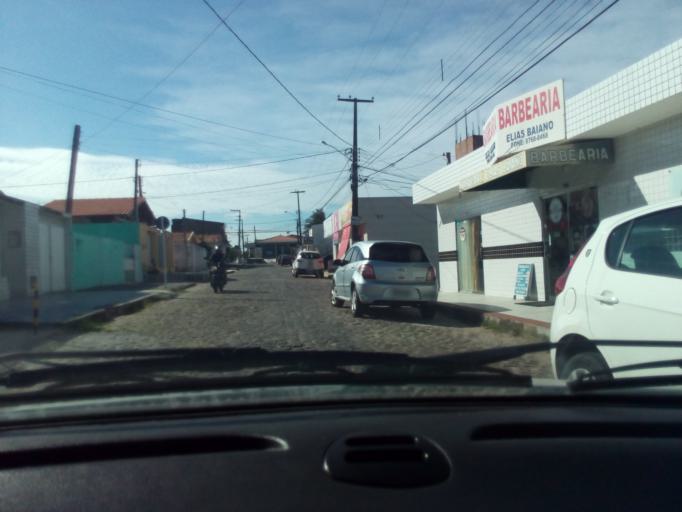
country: BR
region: Rio Grande do Norte
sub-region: Parnamirim
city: Parnamirim
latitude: -5.8870
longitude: -35.2016
